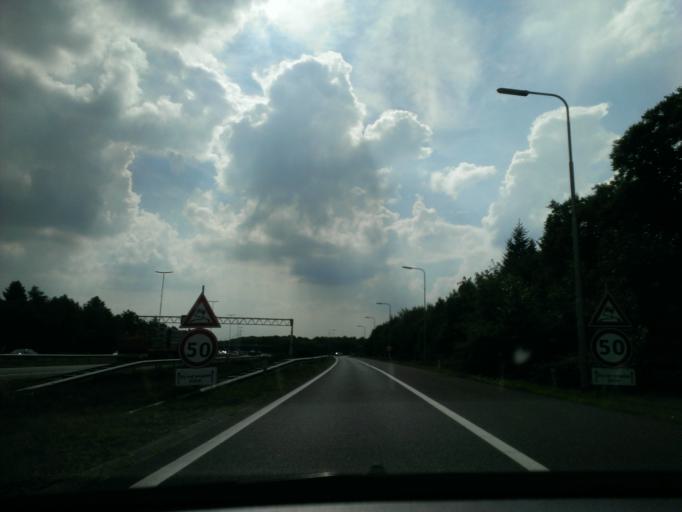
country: NL
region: North Holland
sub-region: Gemeente Hilversum
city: Hilversum
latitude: 52.2065
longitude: 5.1996
